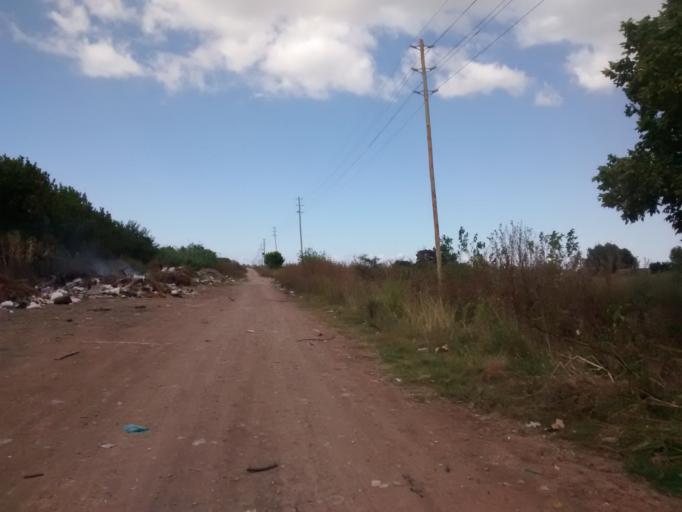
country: AR
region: Buenos Aires
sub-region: Partido de La Plata
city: La Plata
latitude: -34.9718
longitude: -57.9404
